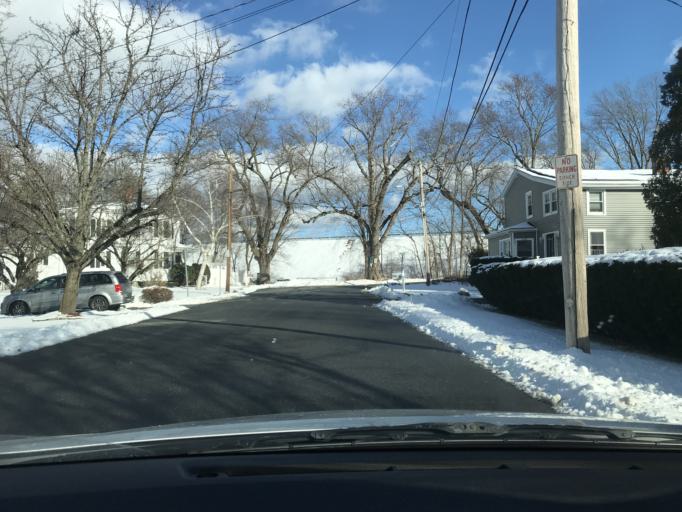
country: US
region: Massachusetts
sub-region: Essex County
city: Saugus
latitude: 42.4919
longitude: -71.0098
